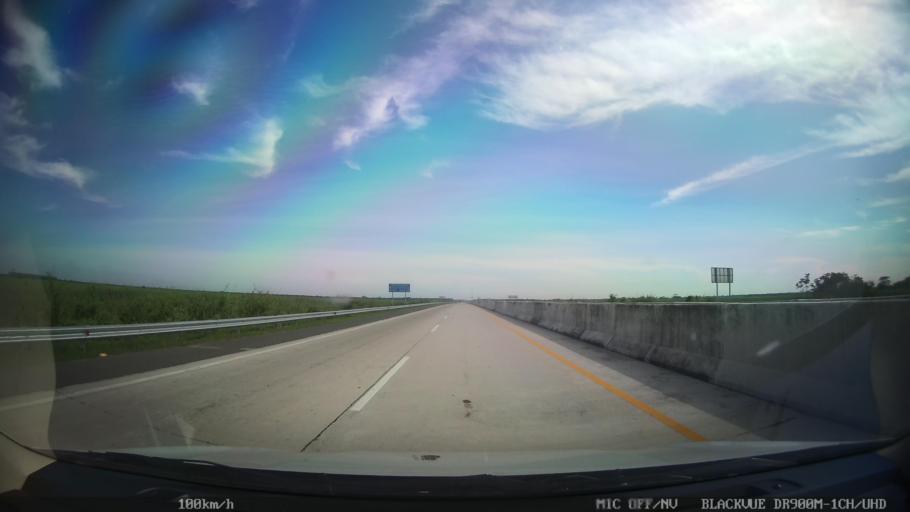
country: ID
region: North Sumatra
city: Binjai
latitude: 3.6744
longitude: 98.5354
